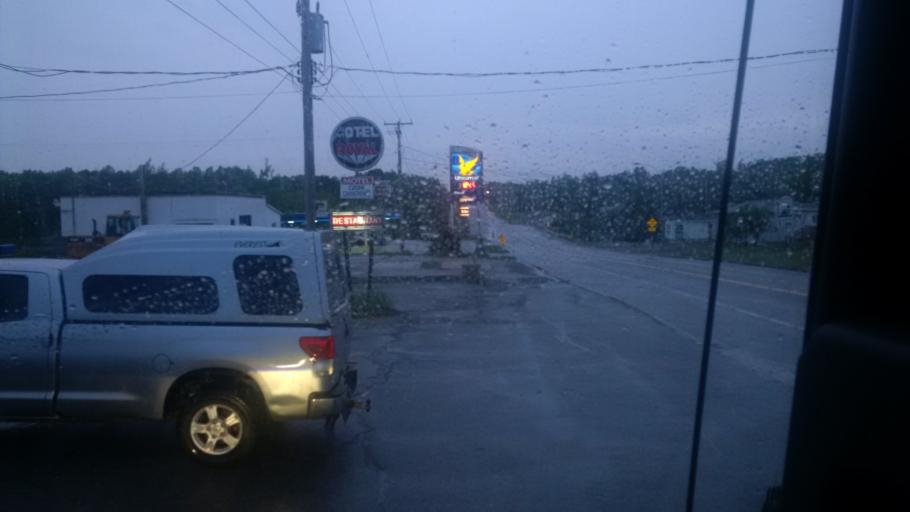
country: CA
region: Quebec
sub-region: Abitibi-Temiscamingue
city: Senneterre
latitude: 48.0717
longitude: -77.3820
